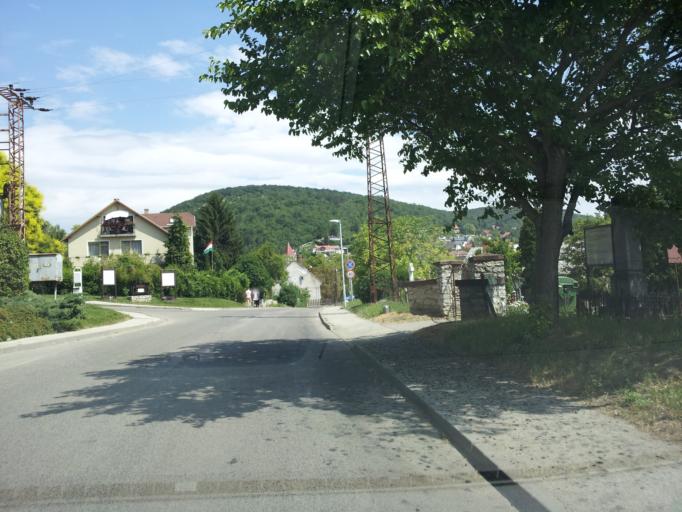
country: HU
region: Veszprem
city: Csopak
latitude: 46.9693
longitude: 17.8956
